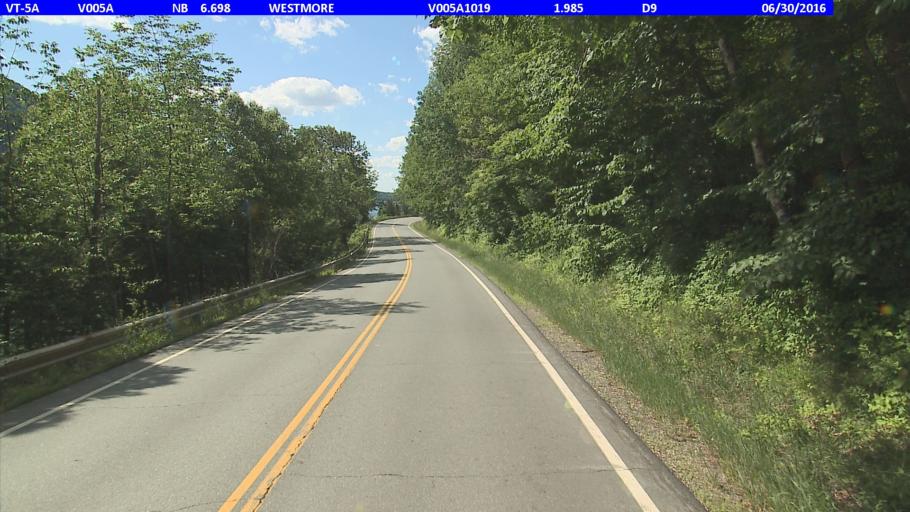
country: US
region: Vermont
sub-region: Caledonia County
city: Lyndonville
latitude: 44.7227
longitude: -72.0321
